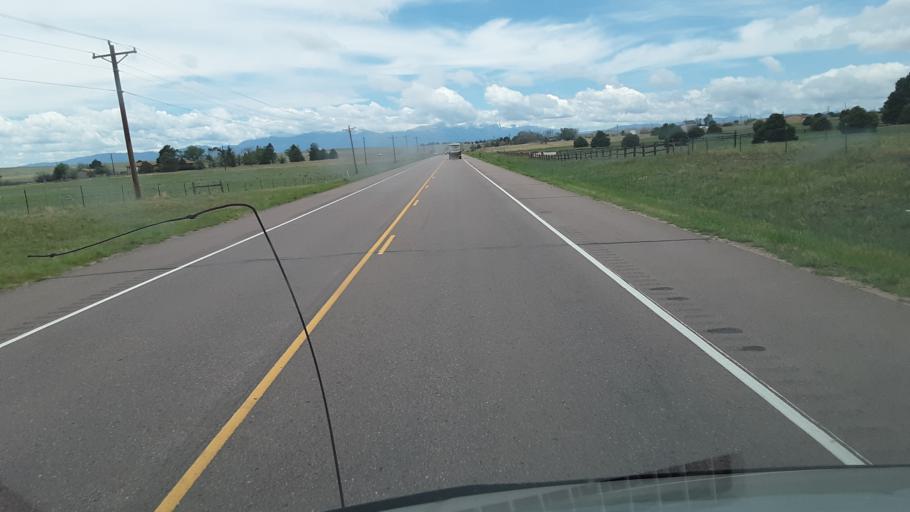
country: US
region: Colorado
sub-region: El Paso County
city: Ellicott
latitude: 38.8386
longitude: -104.5090
